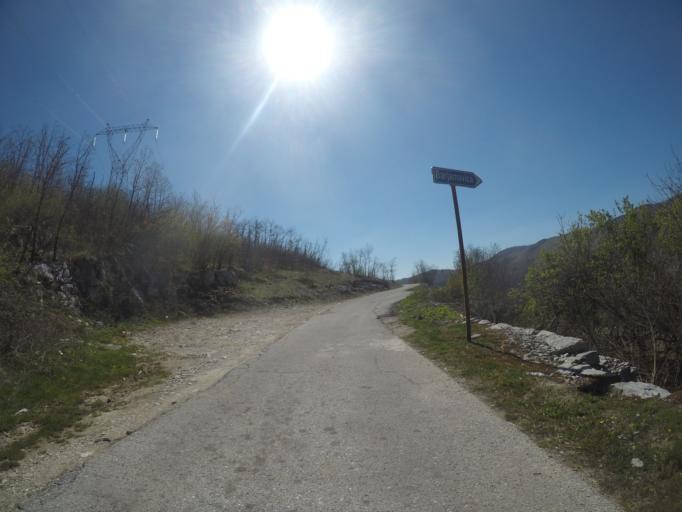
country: ME
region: Cetinje
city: Cetinje
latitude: 42.5279
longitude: 18.9473
